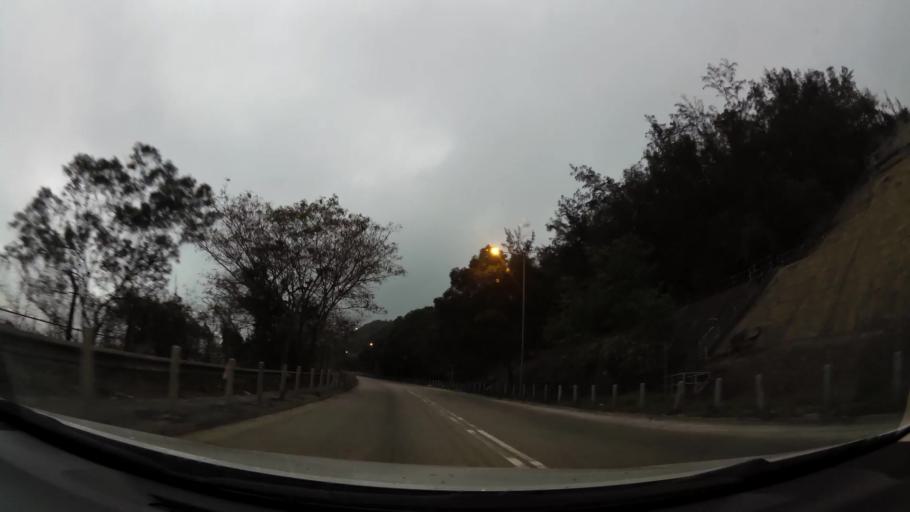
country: HK
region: Tsuen Wan
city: Tsuen Wan
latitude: 22.3317
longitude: 114.0992
